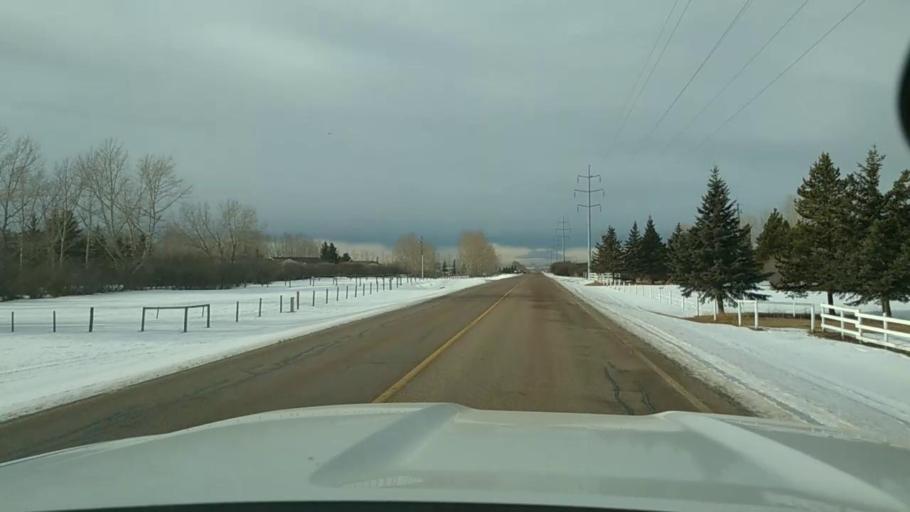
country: CA
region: Alberta
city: Airdrie
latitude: 51.2417
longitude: -113.9766
